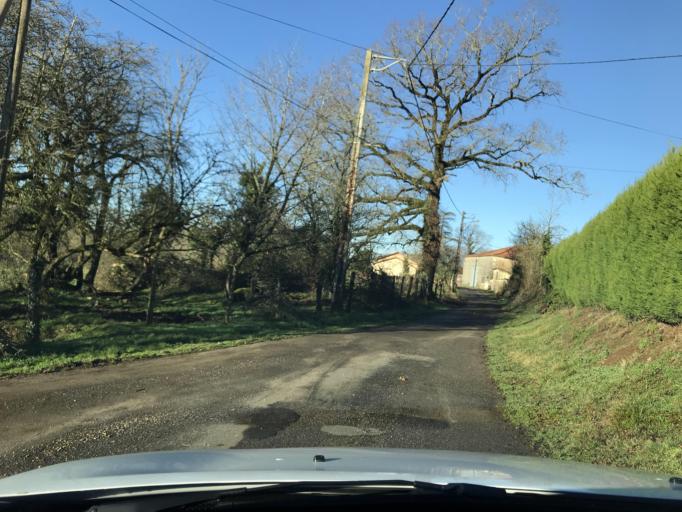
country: FR
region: Poitou-Charentes
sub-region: Departement de la Charente
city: Chasseneuil-sur-Bonnieure
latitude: 45.8403
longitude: 0.5006
